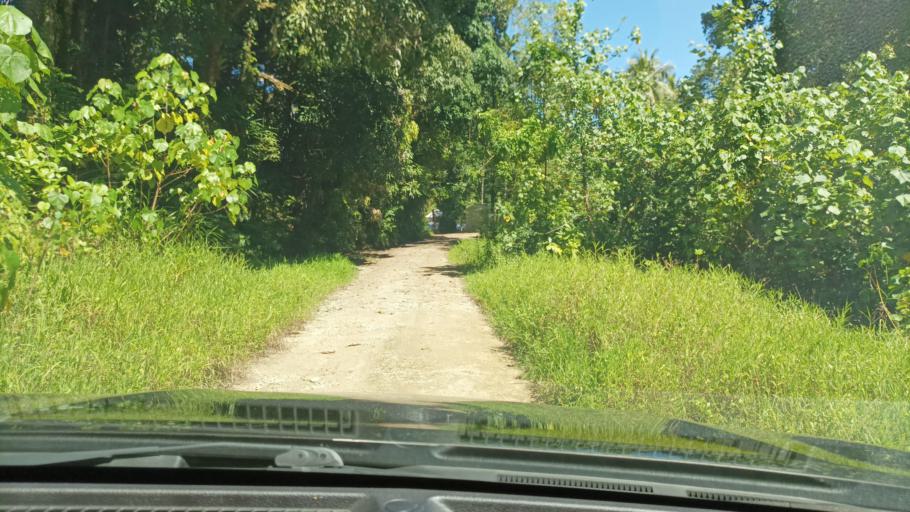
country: FM
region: Pohnpei
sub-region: Madolenihm Municipality
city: Madolenihm Municipality Government
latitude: 6.8449
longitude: 158.3174
